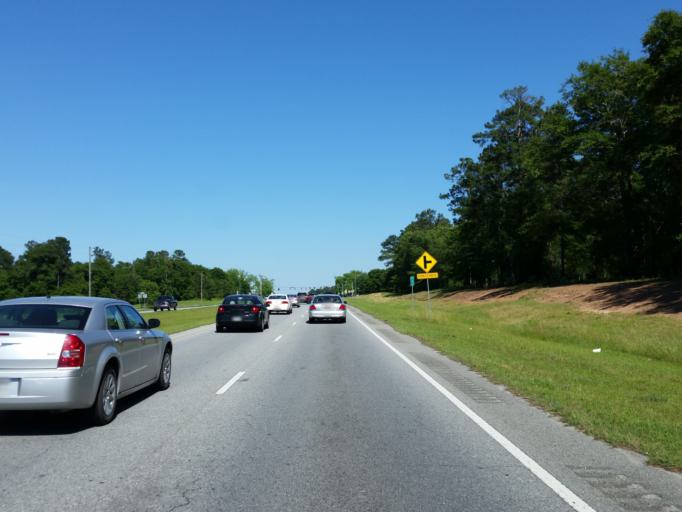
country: US
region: Georgia
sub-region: Lowndes County
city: Valdosta
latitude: 30.8829
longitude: -83.2784
